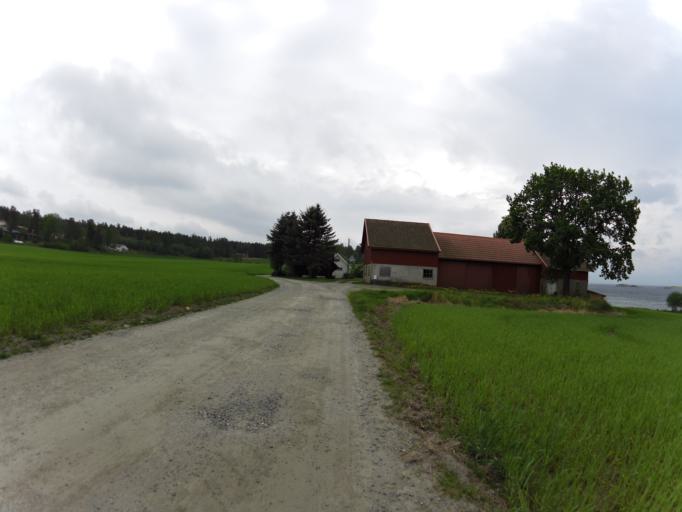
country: NO
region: Ostfold
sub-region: Moss
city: Moss
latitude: 59.4018
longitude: 10.6522
